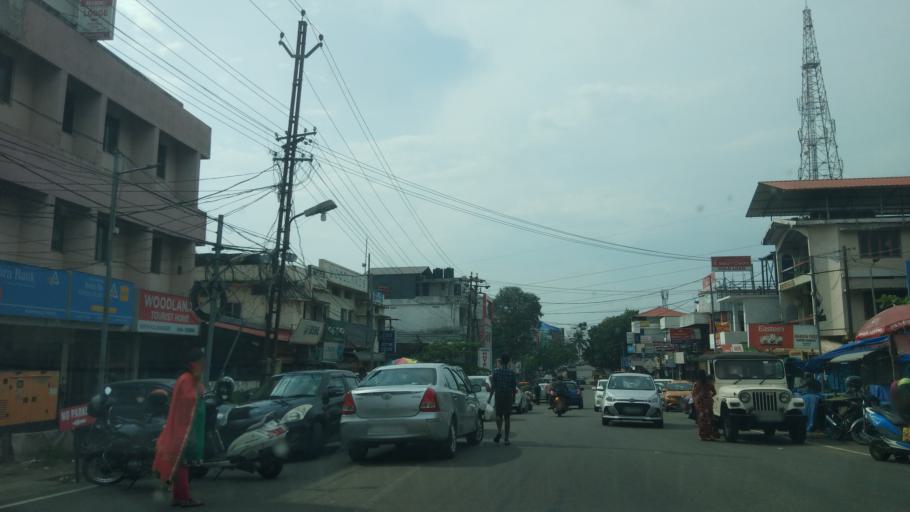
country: IN
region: Kerala
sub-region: Ernakulam
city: Elur
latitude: 10.0619
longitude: 76.3230
